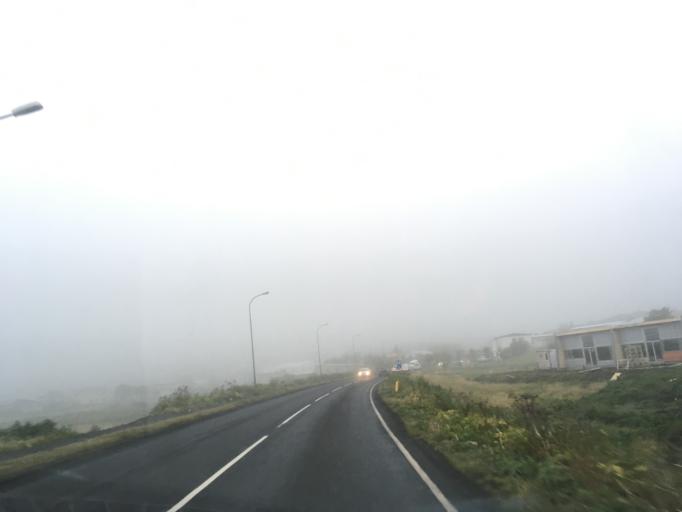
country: IS
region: South
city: Vestmannaeyjar
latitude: 63.4182
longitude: -19.0021
